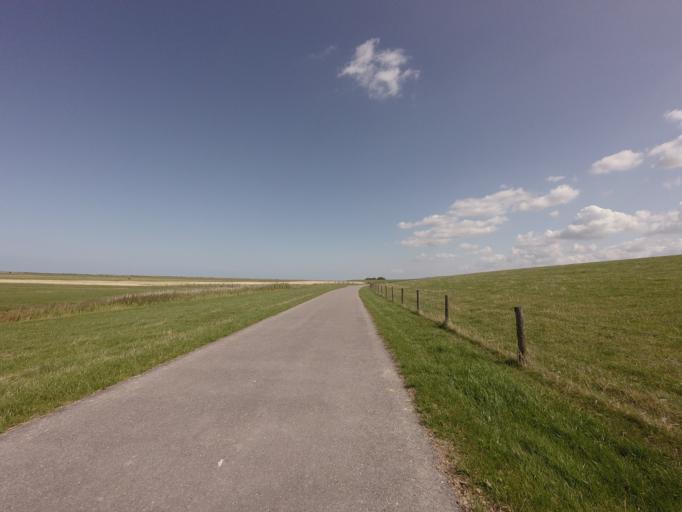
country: NL
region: Friesland
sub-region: Gemeente Ferwerderadiel
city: Marrum
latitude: 53.3429
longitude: 5.7935
